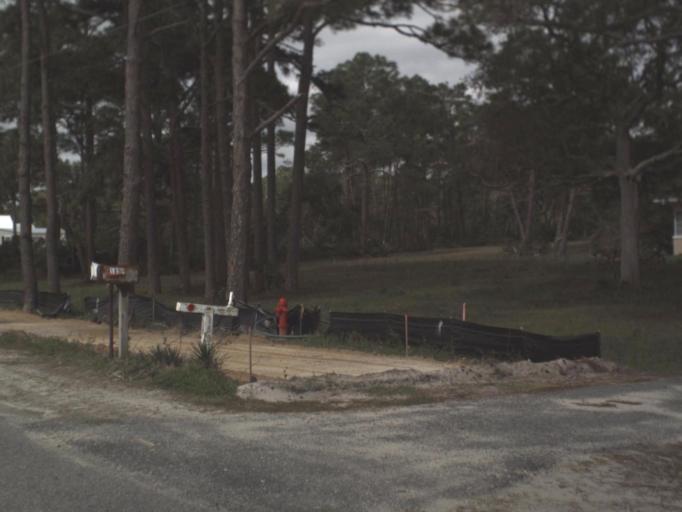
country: US
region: Florida
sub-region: Franklin County
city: Carrabelle
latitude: 29.8283
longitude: -84.6947
